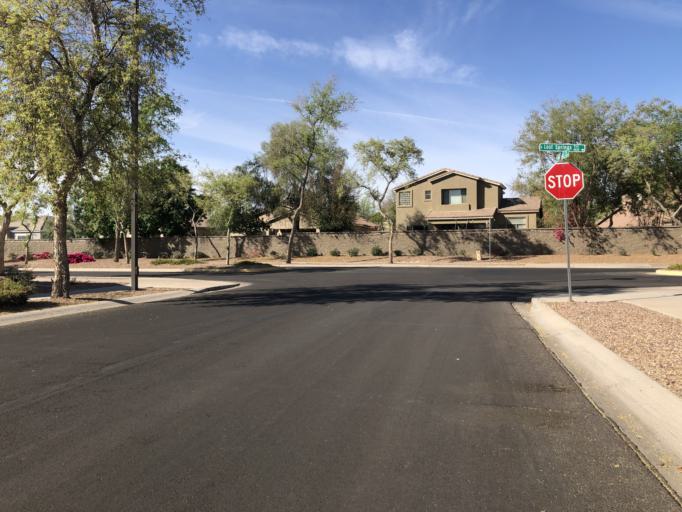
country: US
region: Arizona
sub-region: Maricopa County
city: Queen Creek
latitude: 33.2677
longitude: -111.7003
